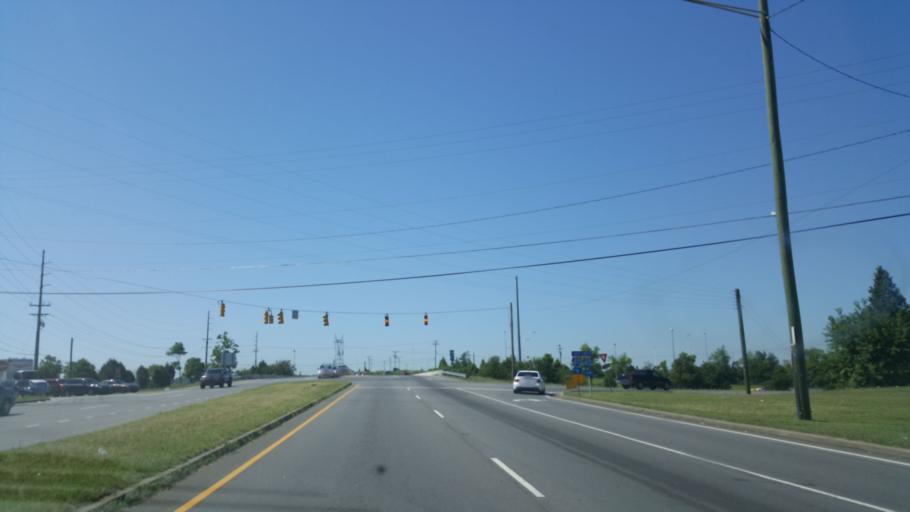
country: US
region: Tennessee
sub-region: Davidson County
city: Lakewood
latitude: 36.1428
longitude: -86.6667
